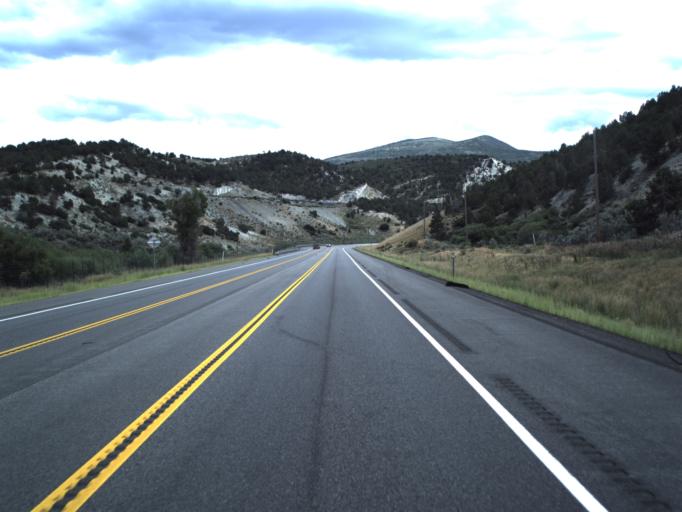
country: US
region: Utah
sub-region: Sanpete County
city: Fairview
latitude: 39.9448
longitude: -111.2044
